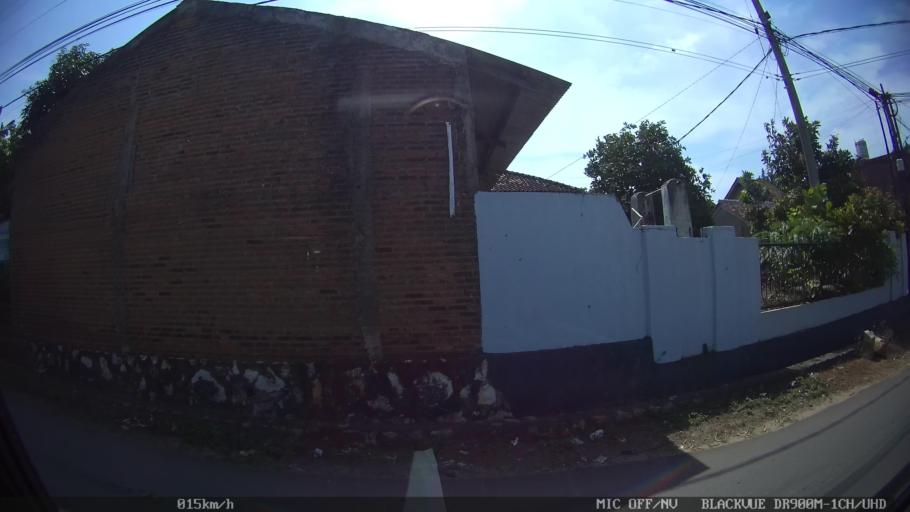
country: ID
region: Lampung
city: Kedaton
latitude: -5.3605
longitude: 105.2505
